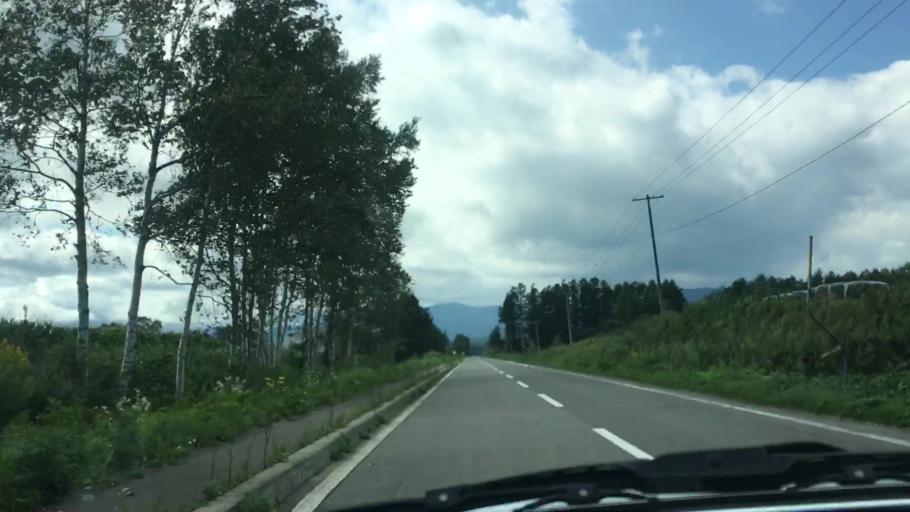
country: JP
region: Hokkaido
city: Otofuke
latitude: 43.2813
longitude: 143.3311
